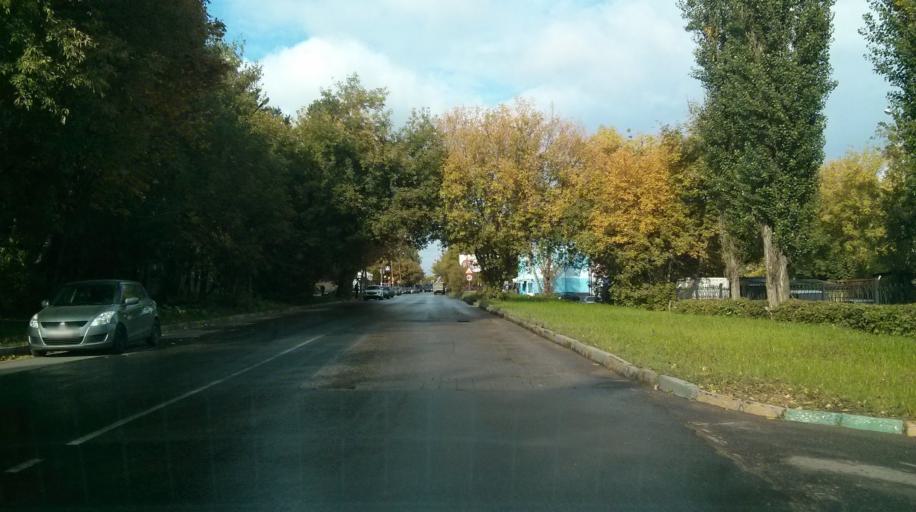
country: RU
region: Nizjnij Novgorod
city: Bor
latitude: 56.3167
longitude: 44.0551
